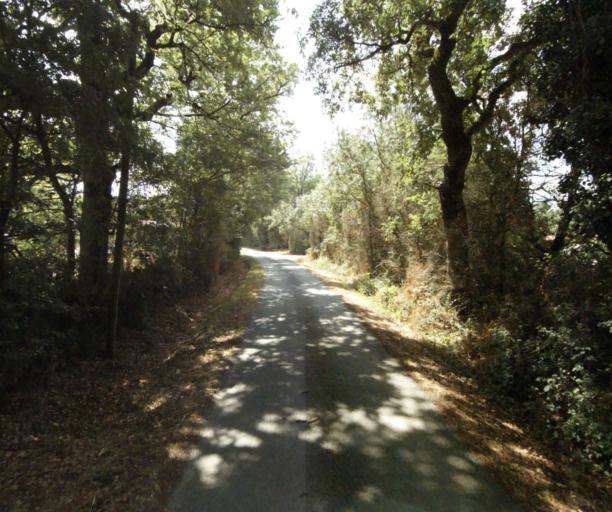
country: FR
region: Midi-Pyrenees
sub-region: Departement du Tarn
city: Dourgne
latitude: 43.4871
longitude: 2.1086
